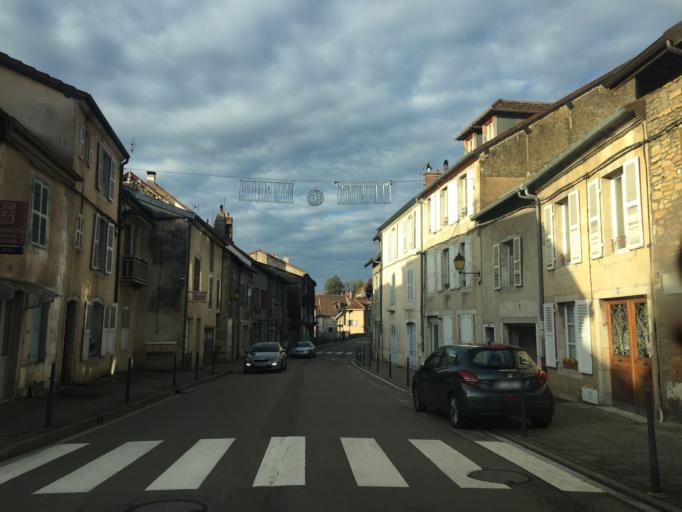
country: FR
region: Franche-Comte
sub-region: Departement du Jura
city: Arbois
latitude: 46.9059
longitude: 5.7700
